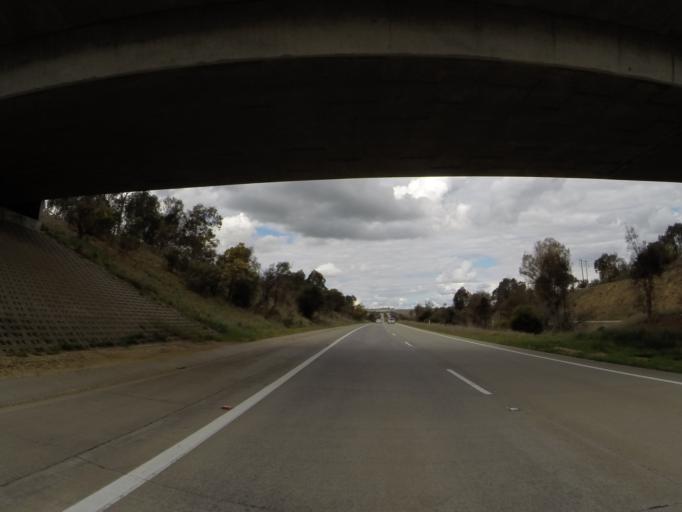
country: AU
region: New South Wales
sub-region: Yass Valley
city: Gundaroo
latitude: -34.7862
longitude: 149.2555
